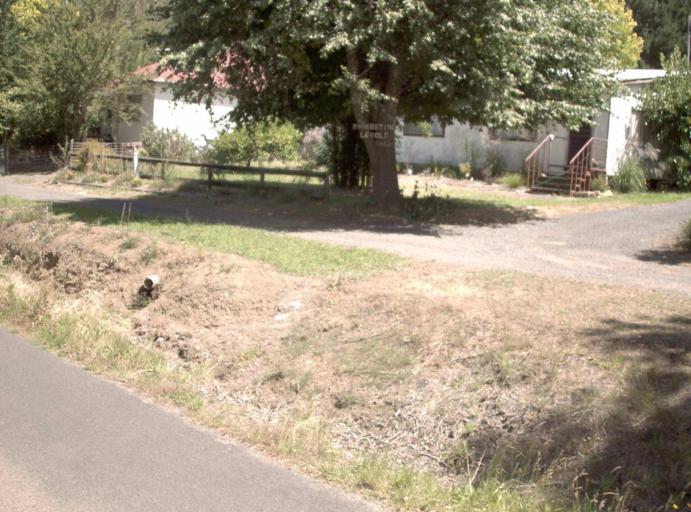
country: AU
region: Victoria
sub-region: Baw Baw
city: Warragul
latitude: -37.8980
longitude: 146.0083
